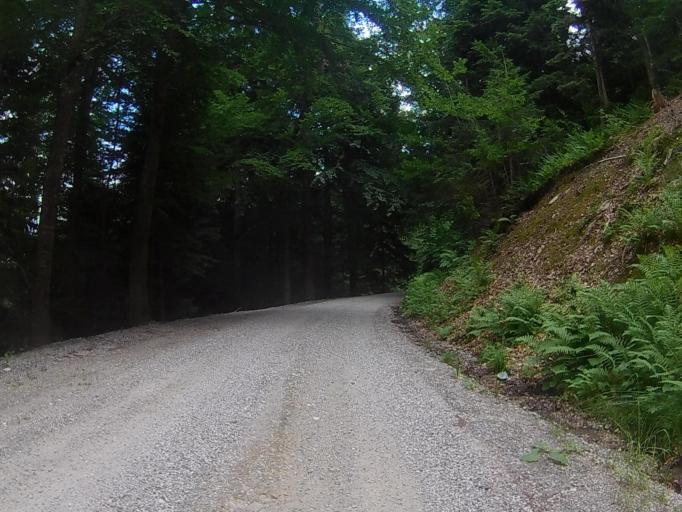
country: SI
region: Ruse
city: Ruse
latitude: 46.5099
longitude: 15.5026
